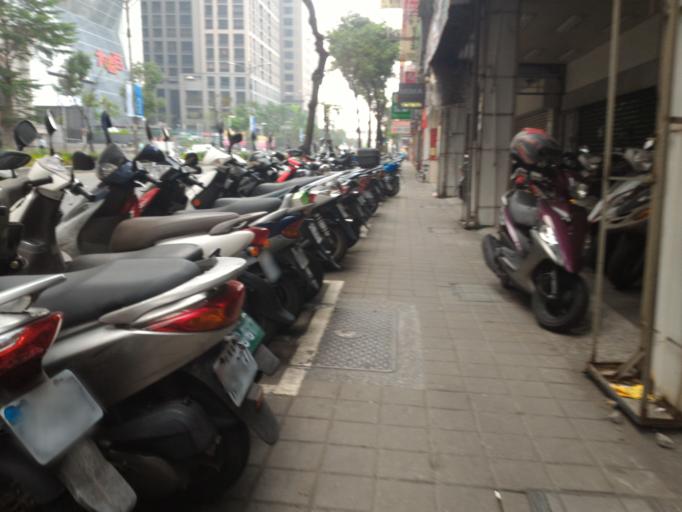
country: TW
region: Taipei
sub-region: Taipei
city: Banqiao
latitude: 25.0137
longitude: 121.4683
